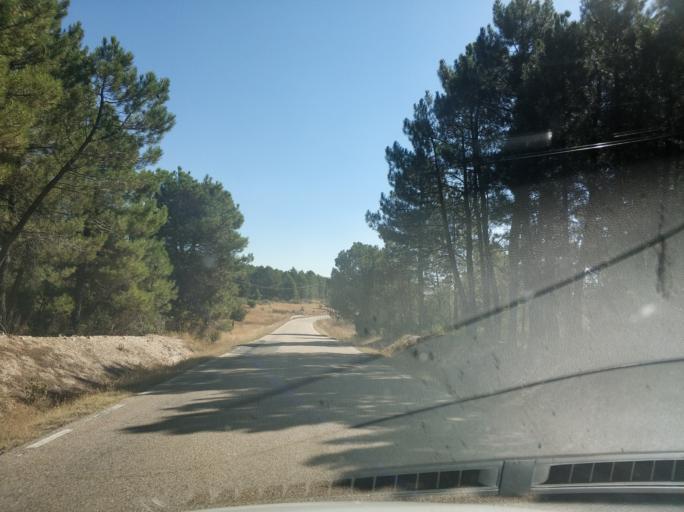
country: ES
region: Castille and Leon
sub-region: Provincia de Soria
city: Santa Maria de las Hoyas
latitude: 41.7761
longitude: -3.1807
